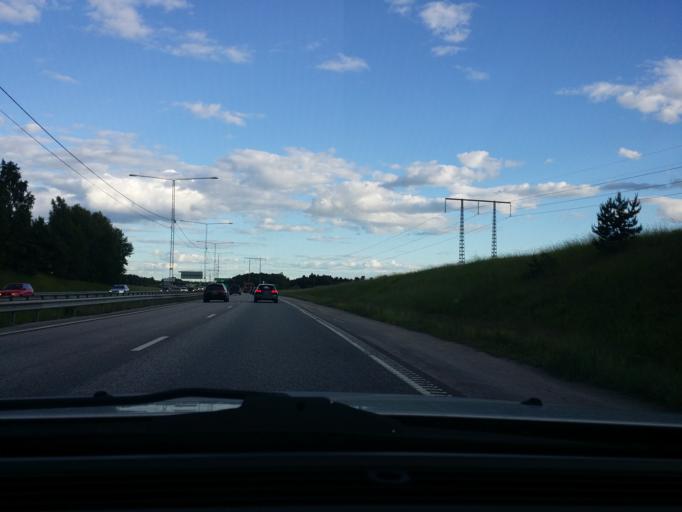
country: SE
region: Stockholm
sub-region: Sigtuna Kommun
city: Rosersberg
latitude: 59.5933
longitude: 17.8961
